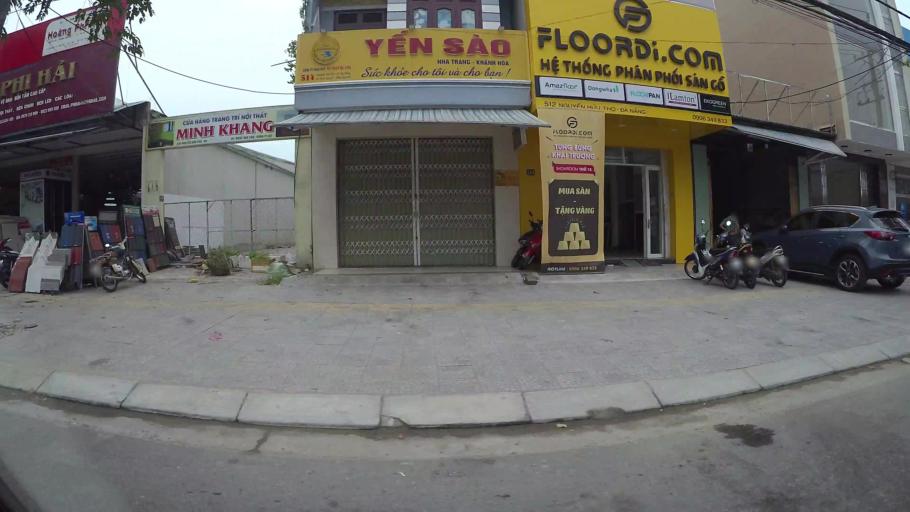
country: VN
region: Da Nang
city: Cam Le
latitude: 16.0289
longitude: 108.2086
